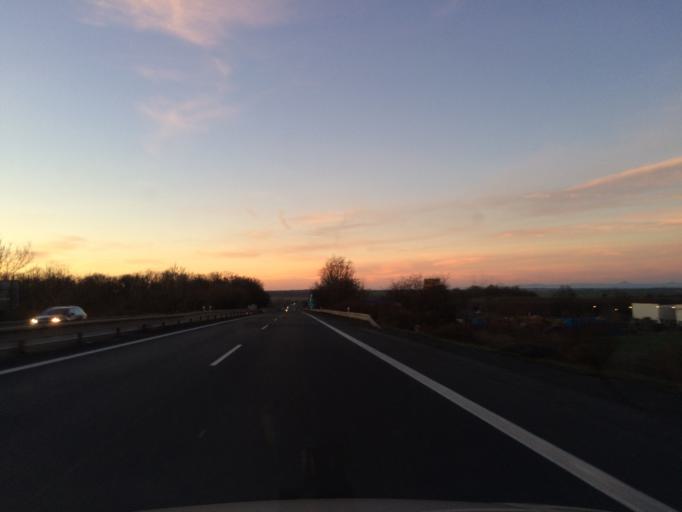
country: CZ
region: Central Bohemia
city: Tuchomerice
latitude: 50.1356
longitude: 14.2485
